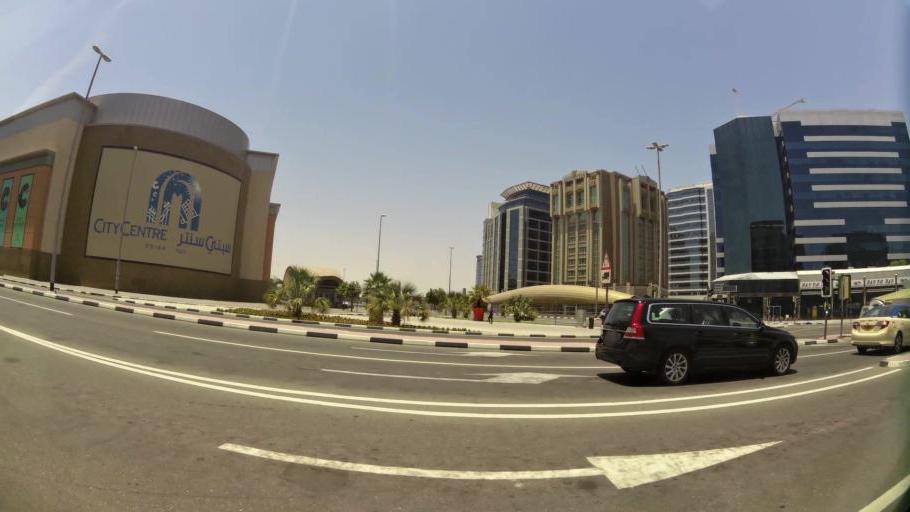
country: AE
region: Ash Shariqah
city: Sharjah
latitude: 25.2548
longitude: 55.3307
